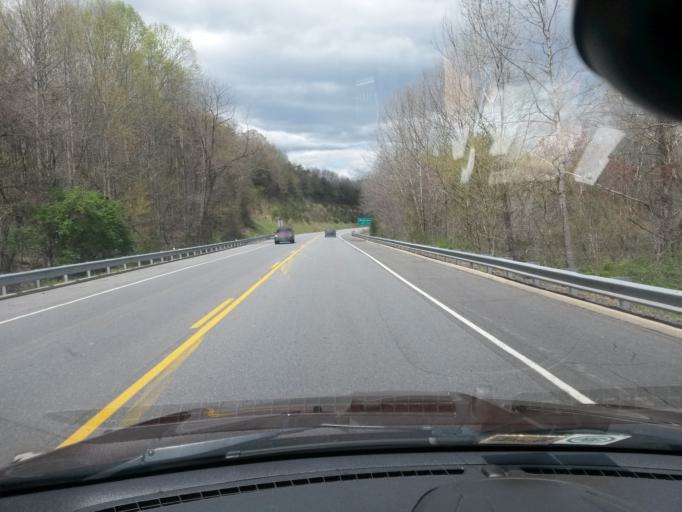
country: US
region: Virginia
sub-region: City of Lynchburg
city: West Lynchburg
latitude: 37.4080
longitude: -79.2292
